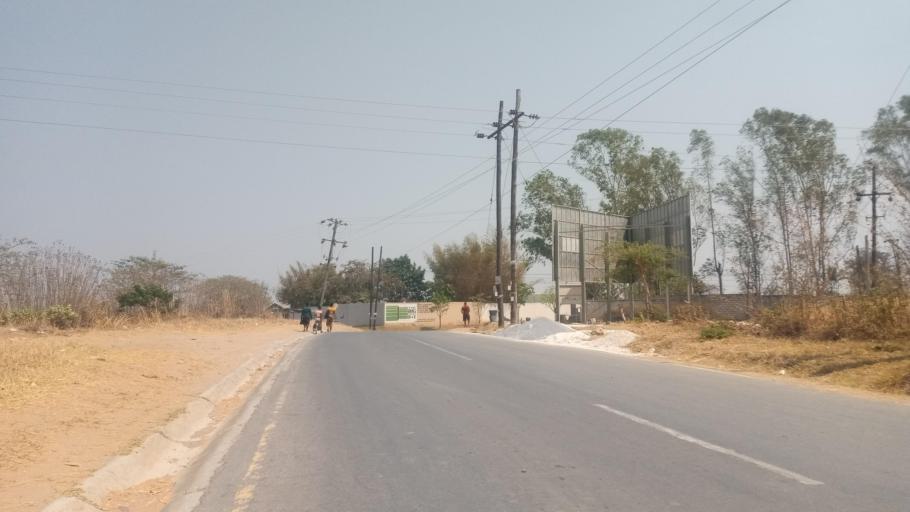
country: ZM
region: Lusaka
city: Lusaka
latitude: -15.4315
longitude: 28.3739
